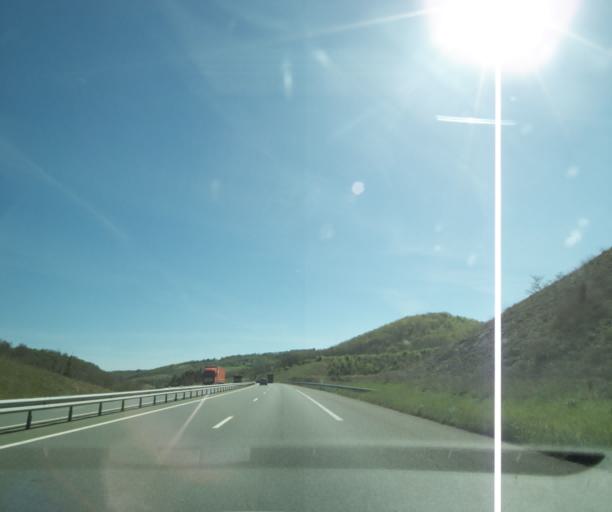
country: FR
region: Midi-Pyrenees
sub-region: Departement du Lot
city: Le Vigan
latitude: 44.7579
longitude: 1.5394
